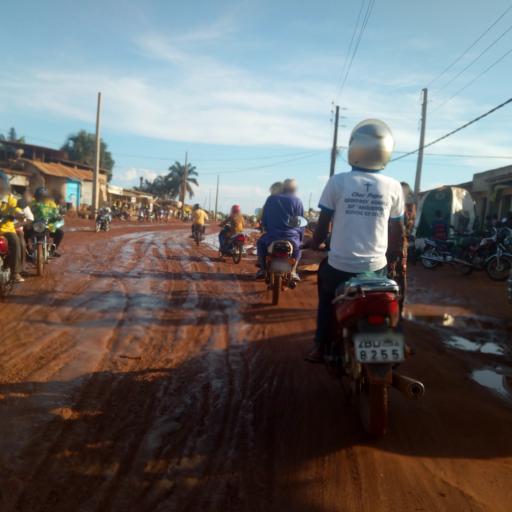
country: BJ
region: Atlantique
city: Hevie
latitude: 6.4002
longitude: 2.2687
